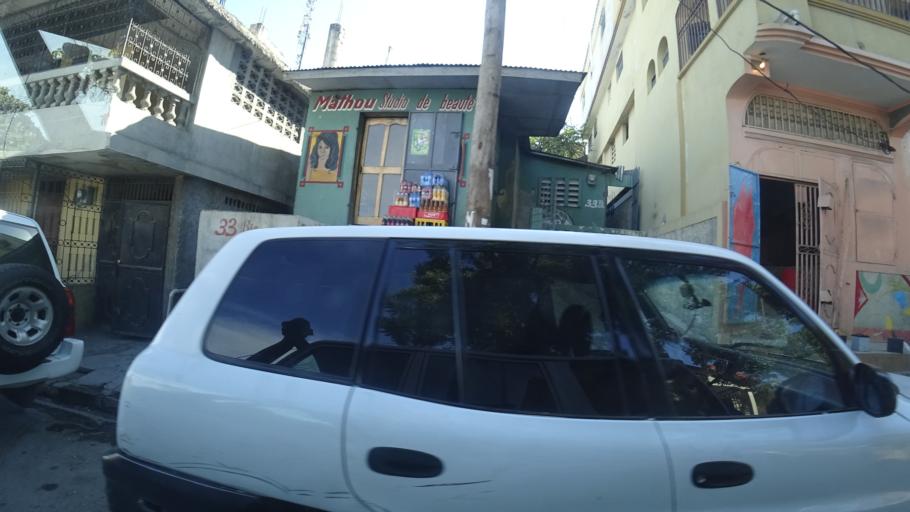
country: HT
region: Ouest
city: Delmas 73
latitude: 18.5484
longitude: -72.3151
